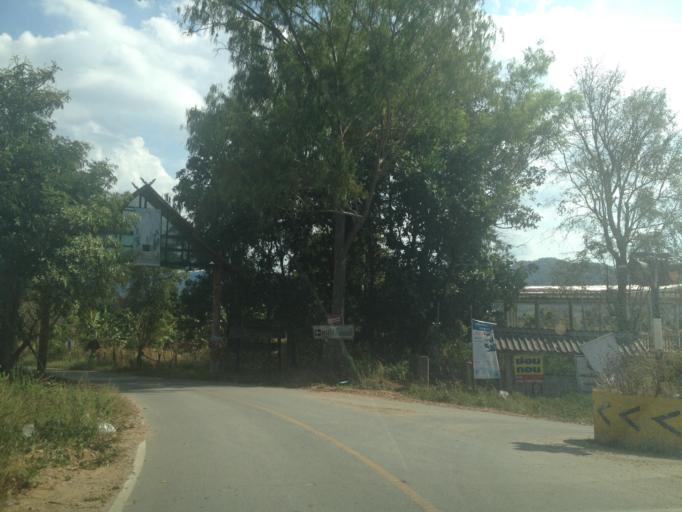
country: TH
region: Mae Hong Son
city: Ban Huai I Huak
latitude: 18.1062
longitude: 98.2202
